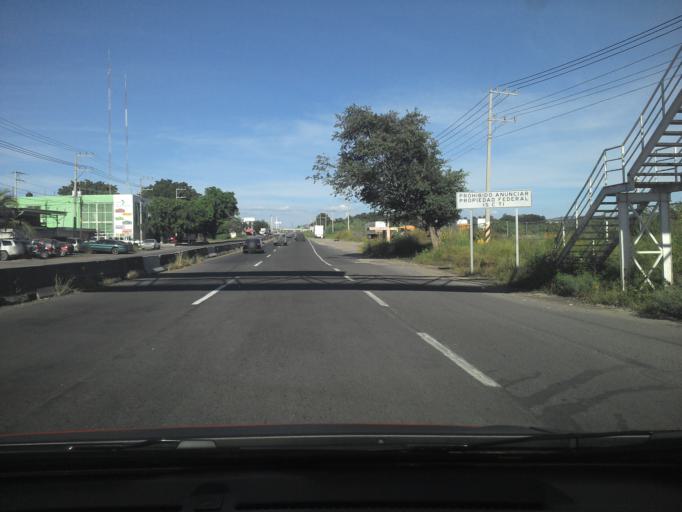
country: MX
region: Jalisco
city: El Refugio
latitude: 20.6667
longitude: -103.7193
